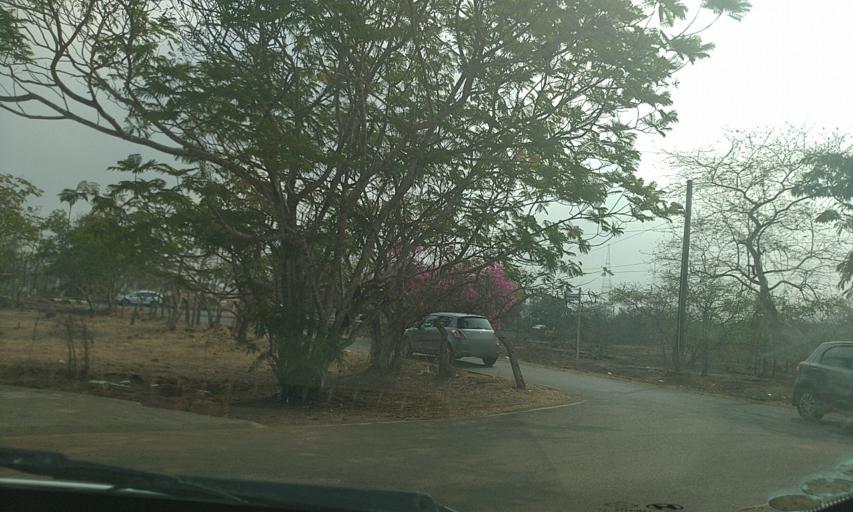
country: IN
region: Goa
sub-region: North Goa
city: Taleigao
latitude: 15.4563
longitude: 73.8350
